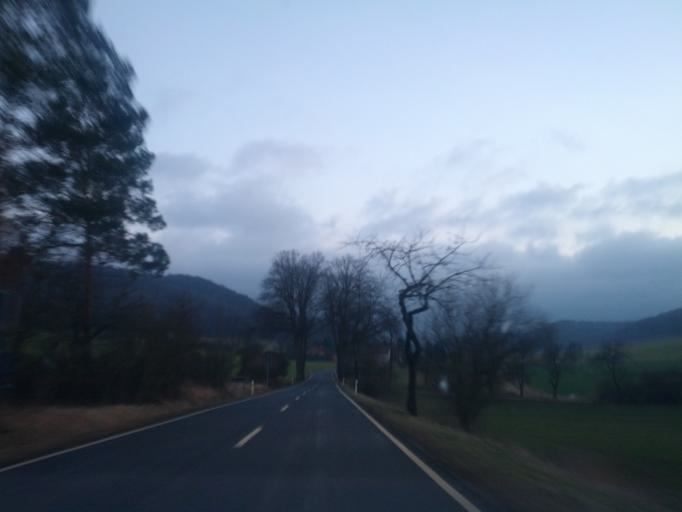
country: DE
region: Thuringia
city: Ifta
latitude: 51.0825
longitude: 10.2159
